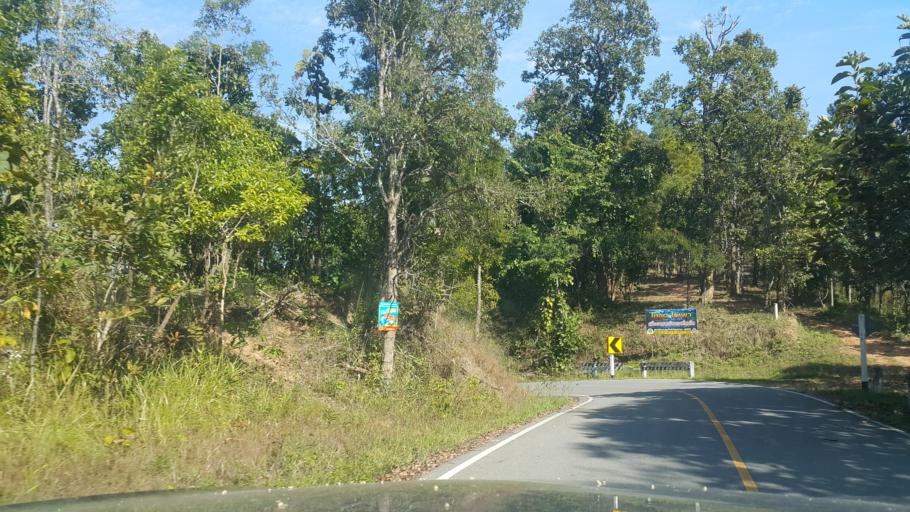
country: TH
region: Chiang Mai
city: Samoeng
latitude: 18.9081
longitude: 98.6758
